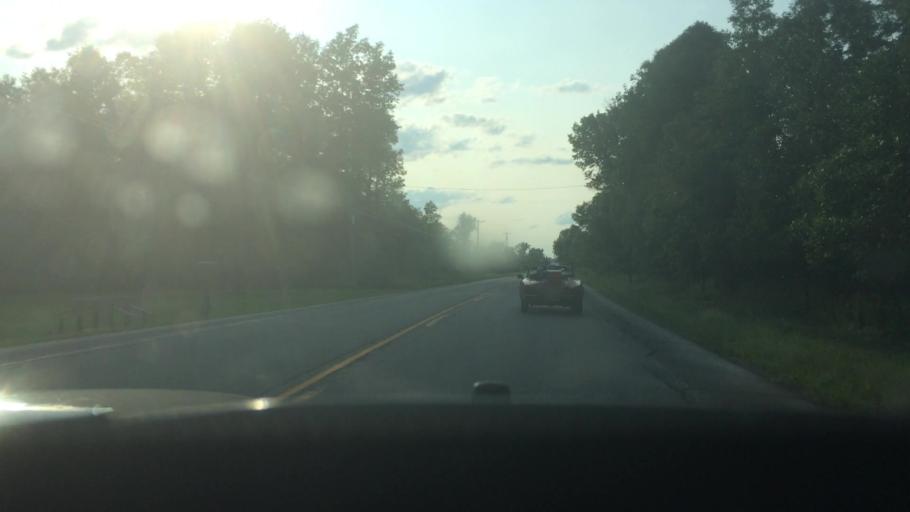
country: US
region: New York
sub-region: St. Lawrence County
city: Canton
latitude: 44.6501
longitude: -75.2967
